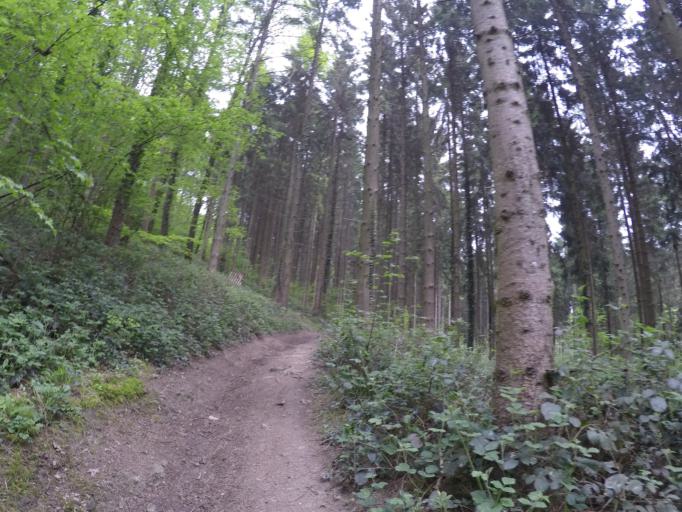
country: BE
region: Wallonia
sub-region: Province de Namur
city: Yvoir
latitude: 50.3343
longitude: 4.9424
